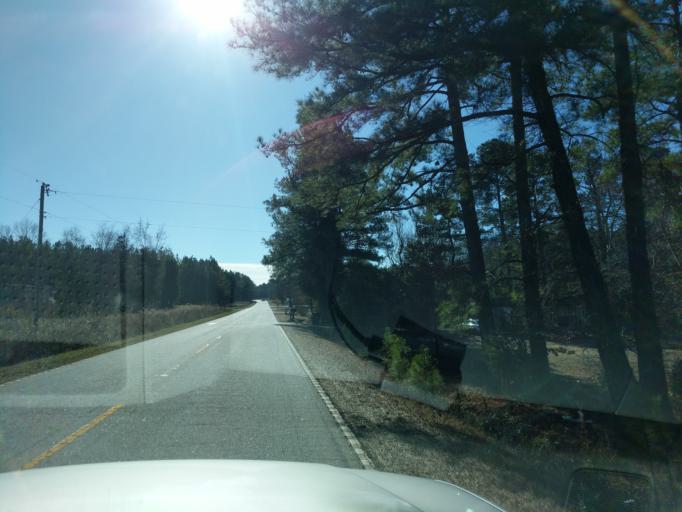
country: US
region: South Carolina
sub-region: Laurens County
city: Joanna
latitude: 34.3395
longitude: -81.8544
